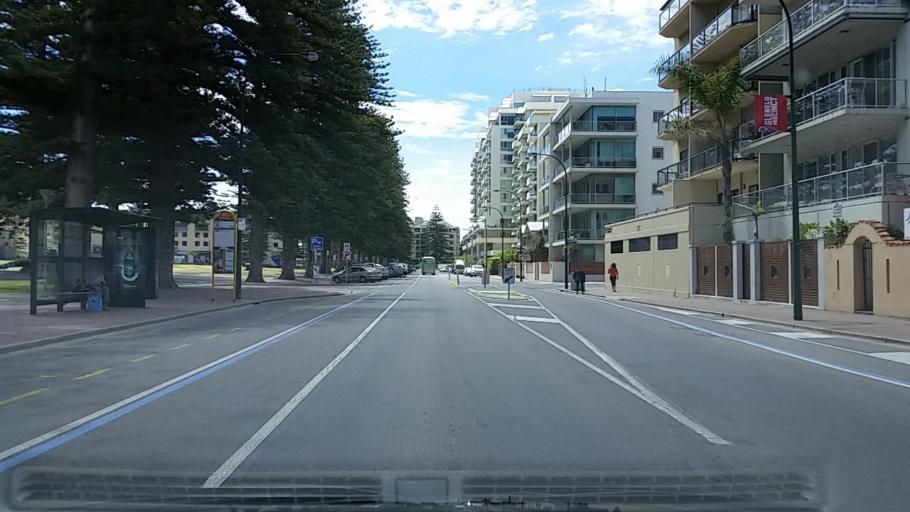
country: AU
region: South Australia
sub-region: Adelaide
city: Glenelg
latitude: -34.9791
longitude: 138.5124
